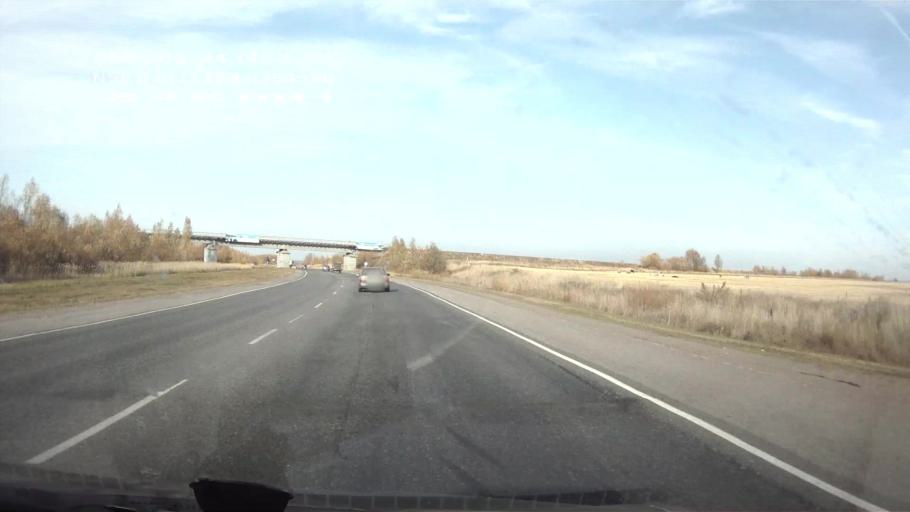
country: RU
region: Chuvashia
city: Kugesi
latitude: 56.0402
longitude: 47.3643
